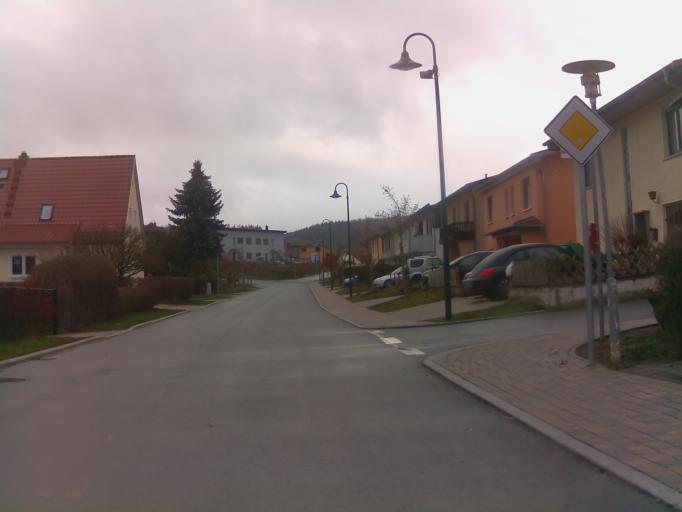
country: DE
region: Thuringia
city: Juchsen
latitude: 50.4783
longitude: 10.4971
